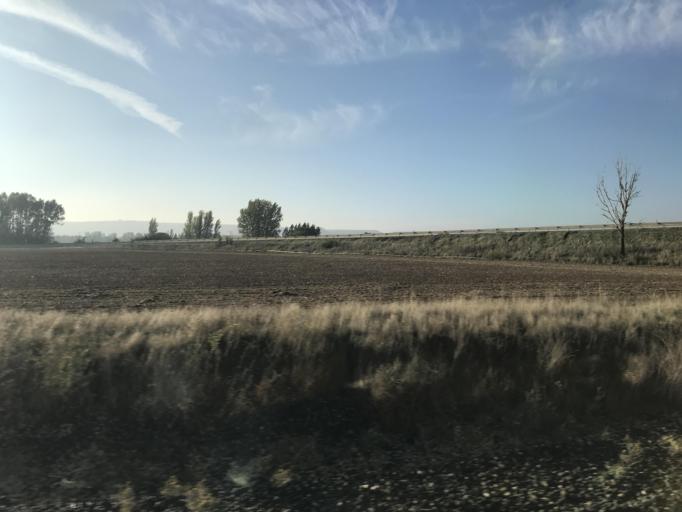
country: ES
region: Castille and Leon
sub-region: Provincia de Palencia
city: Reinoso de Cerrato
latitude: 41.9876
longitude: -4.4107
